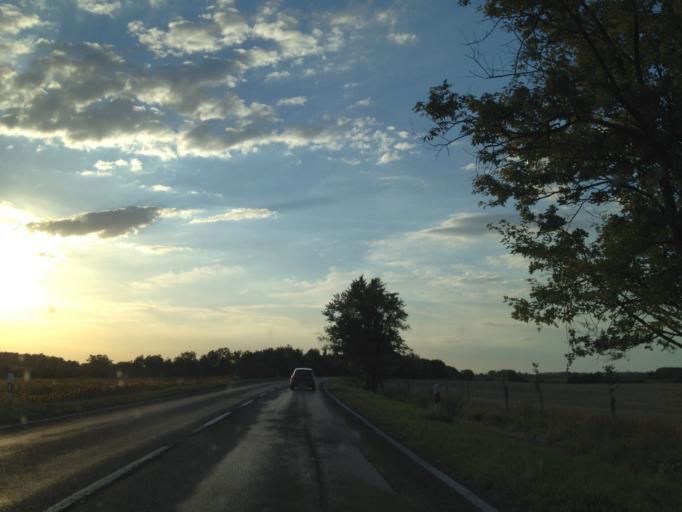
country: HU
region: Gyor-Moson-Sopron
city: Mosonszentmiklos
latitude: 47.7739
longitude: 17.4216
